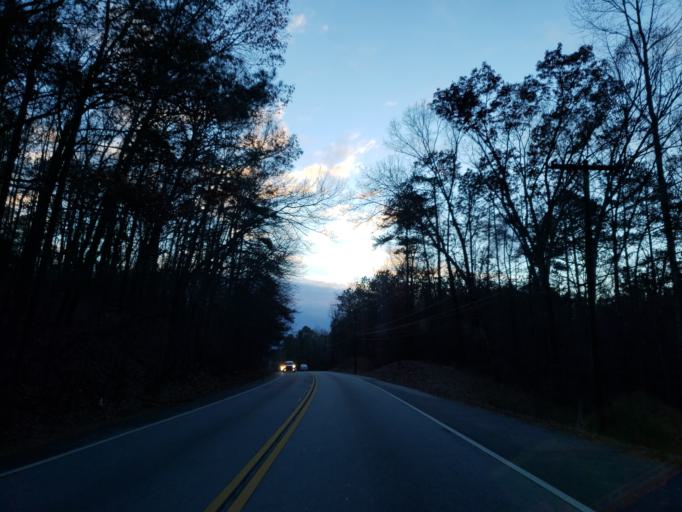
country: US
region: Georgia
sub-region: Fulton County
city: Union City
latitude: 33.6975
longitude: -84.5846
